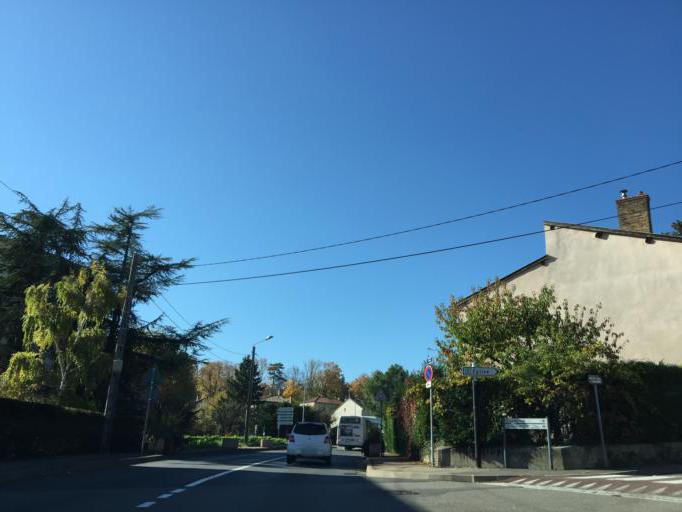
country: FR
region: Rhone-Alpes
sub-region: Departement du Rhone
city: Saint-Genis-Laval
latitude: 45.6932
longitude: 4.7964
